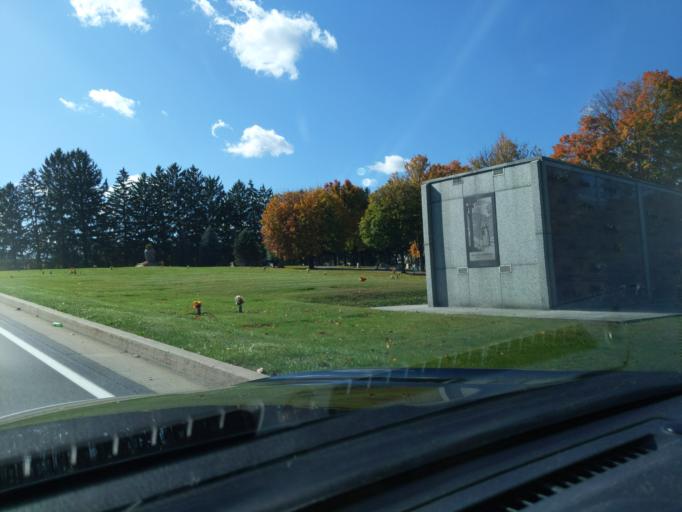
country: US
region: Pennsylvania
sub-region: Blair County
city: Lakemont
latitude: 40.4550
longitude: -78.4100
